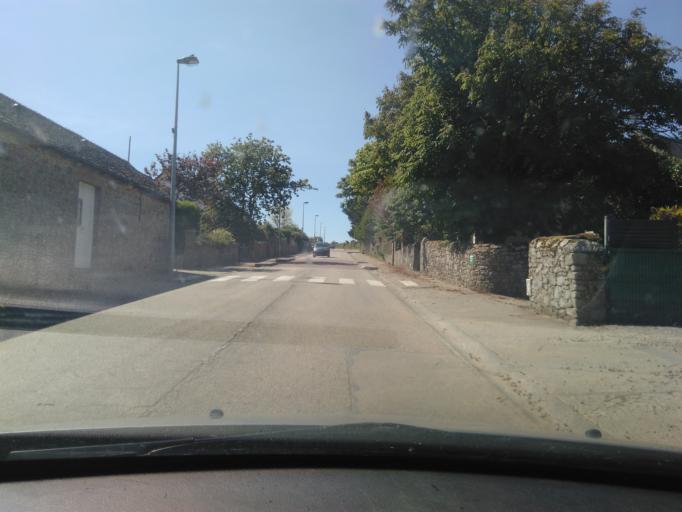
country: FR
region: Lower Normandy
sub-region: Departement de la Manche
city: Beaumont-Hague
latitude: 49.7105
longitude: -1.9321
